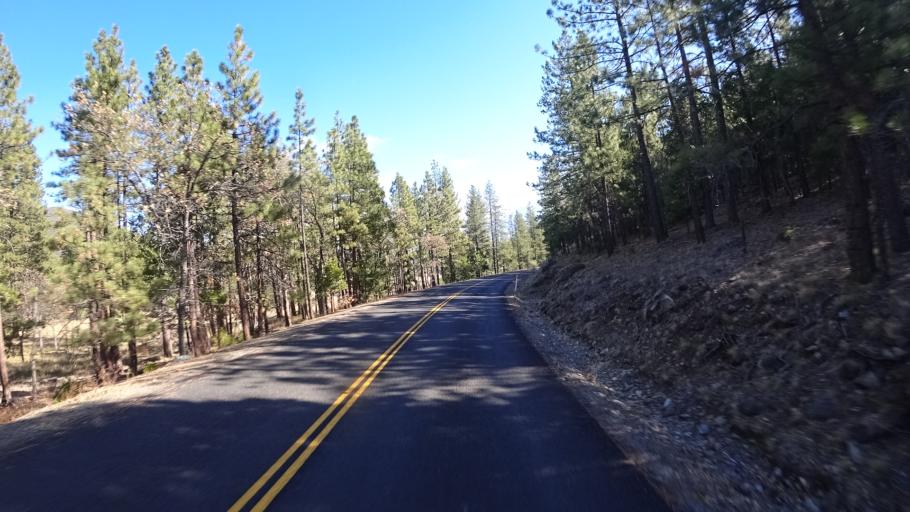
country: US
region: California
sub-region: Siskiyou County
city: Weed
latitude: 41.4330
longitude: -122.4929
